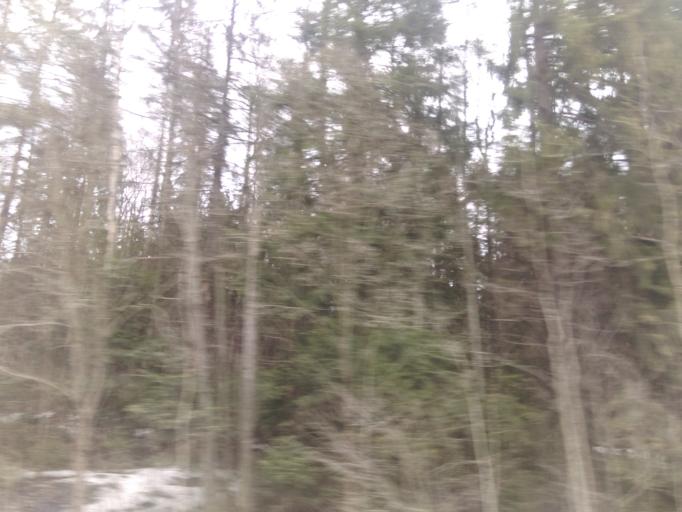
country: RU
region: Moskovskaya
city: Kolyubakino
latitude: 55.6260
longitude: 36.5330
